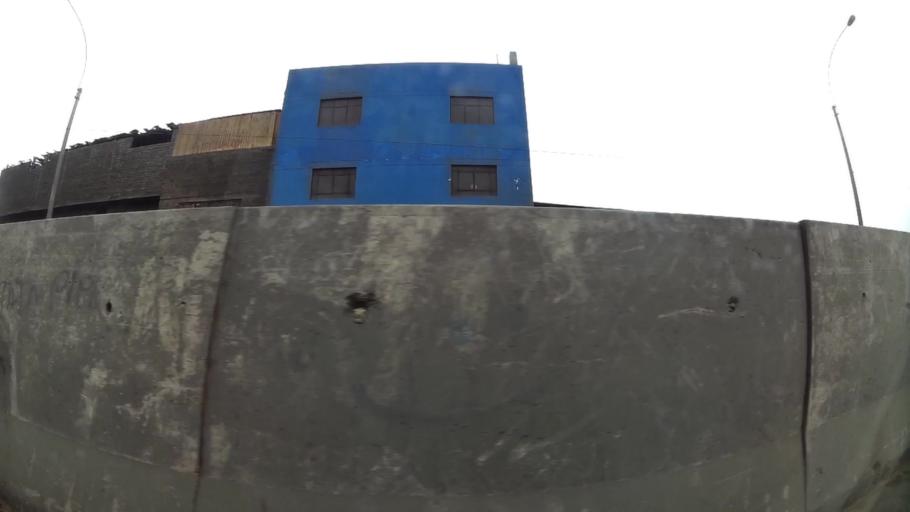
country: PE
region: Lima
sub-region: Lima
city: San Luis
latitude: -12.0621
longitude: -77.0044
